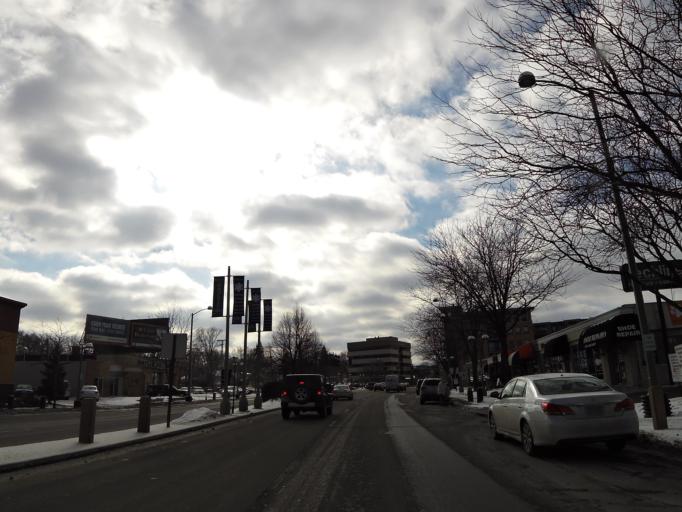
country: US
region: Minnesota
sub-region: Hennepin County
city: Saint Louis Park
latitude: 44.9352
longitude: -93.3359
